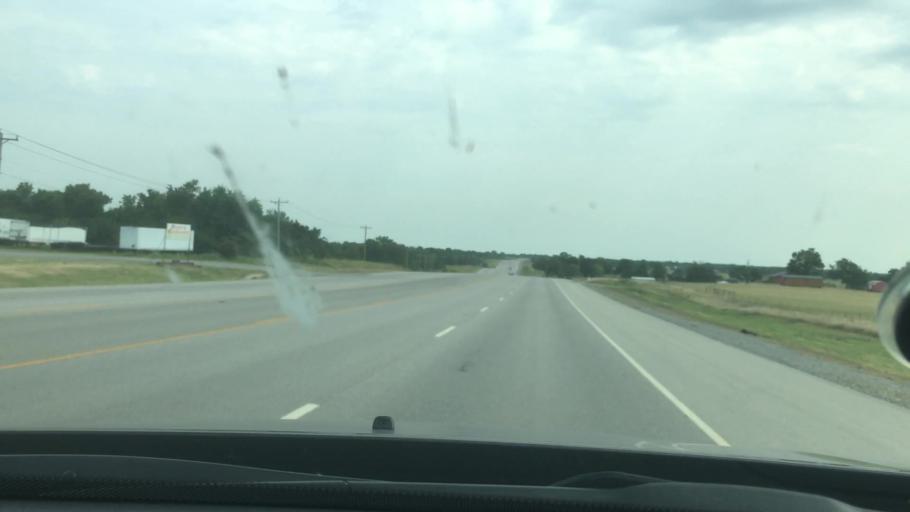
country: US
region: Oklahoma
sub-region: Bryan County
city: Durant
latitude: 34.0579
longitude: -96.3726
